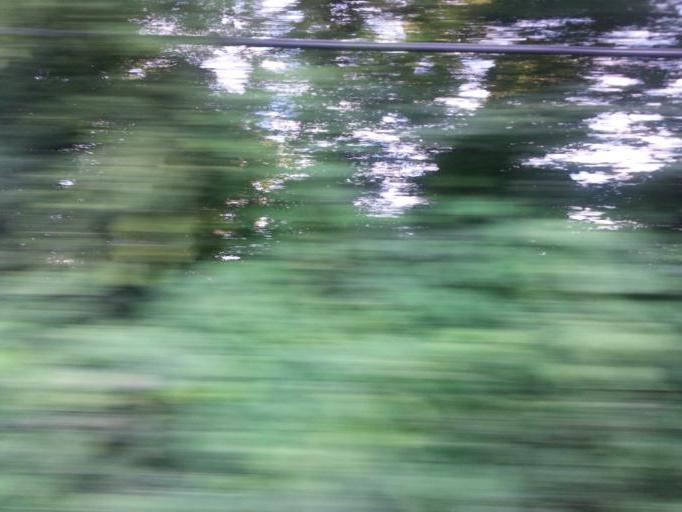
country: US
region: Tennessee
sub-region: Knox County
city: Mascot
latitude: 36.0344
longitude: -83.8240
